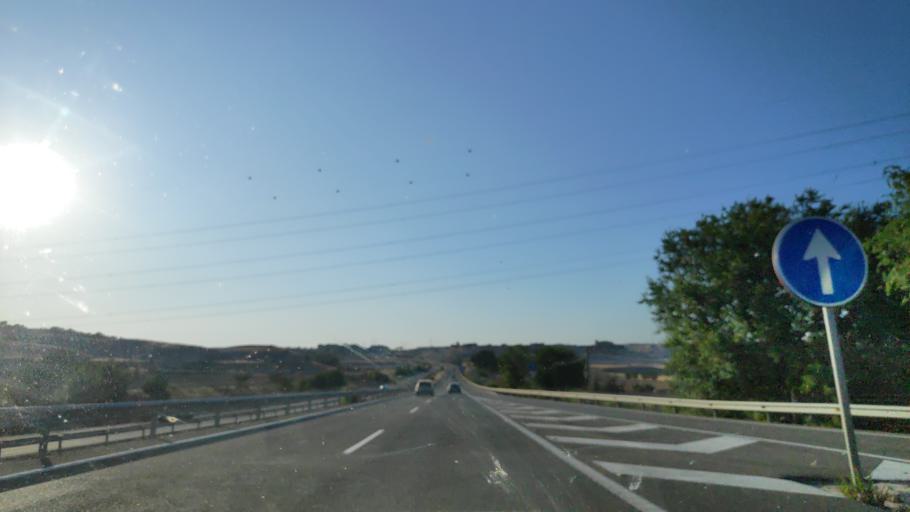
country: ES
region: Castille-La Mancha
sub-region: Provincia de Cuenca
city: Belinchon
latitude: 40.0349
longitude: -3.0446
